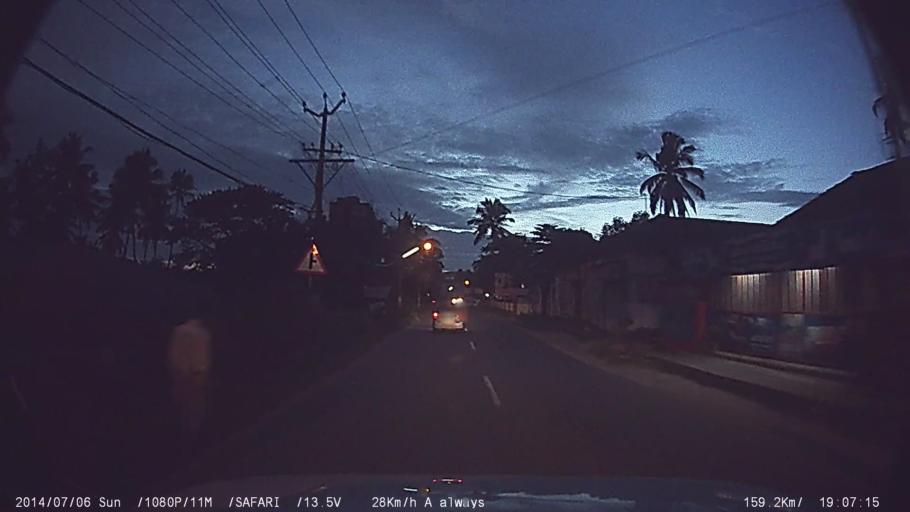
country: IN
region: Kerala
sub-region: Palakkad district
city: Palakkad
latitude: 10.7496
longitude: 76.6515
